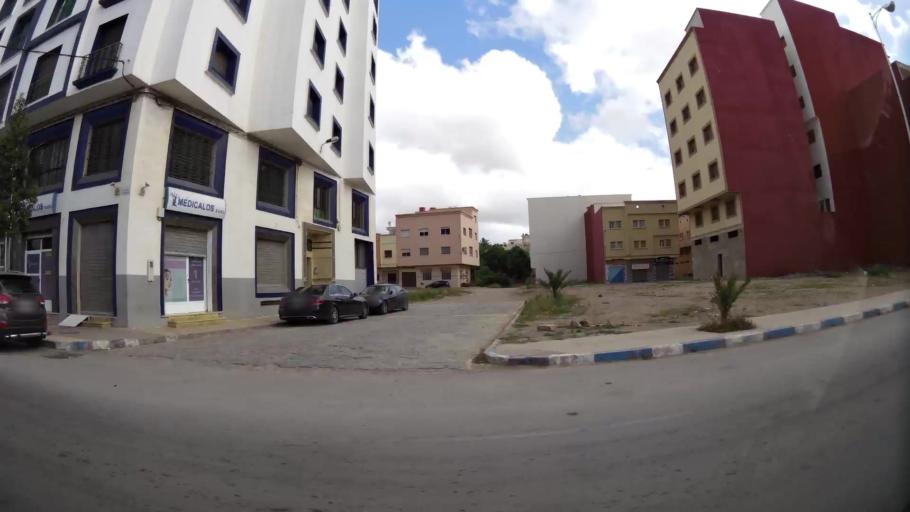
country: MA
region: Oriental
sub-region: Nador
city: Nador
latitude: 35.1610
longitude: -2.9291
